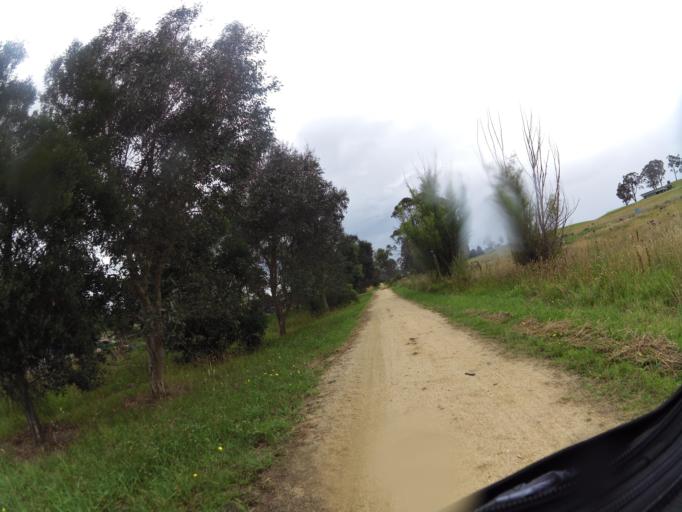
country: AU
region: Victoria
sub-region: East Gippsland
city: Bairnsdale
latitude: -37.7276
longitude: 147.8068
